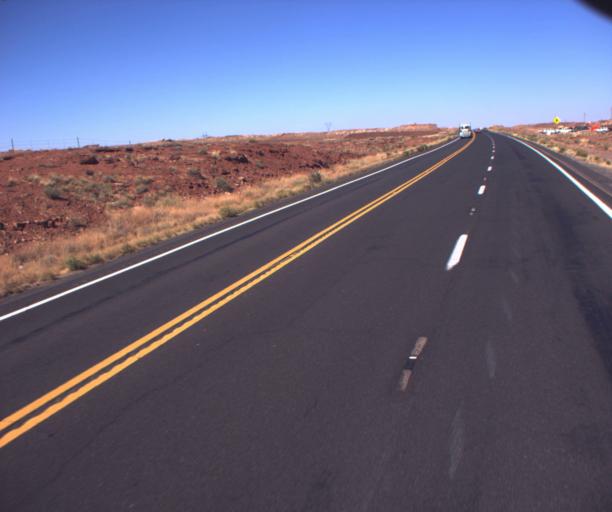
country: US
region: Arizona
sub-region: Coconino County
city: Tuba City
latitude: 35.7928
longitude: -111.4489
